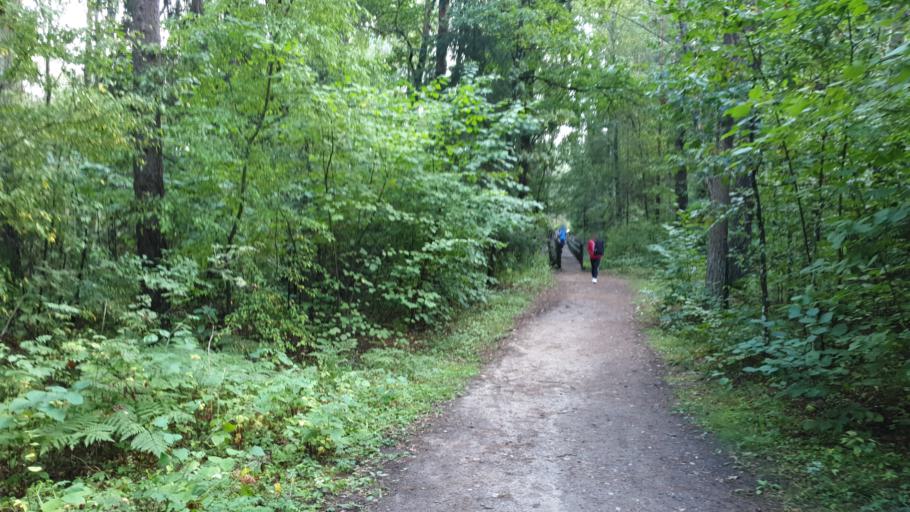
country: LT
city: Trakai
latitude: 54.6452
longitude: 24.9670
